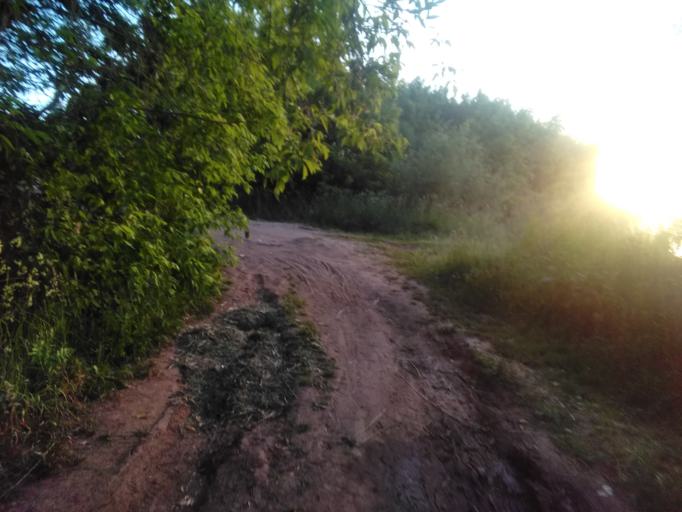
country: RU
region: Udmurtiya
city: Khokhryaki
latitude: 56.8549
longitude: 53.4053
